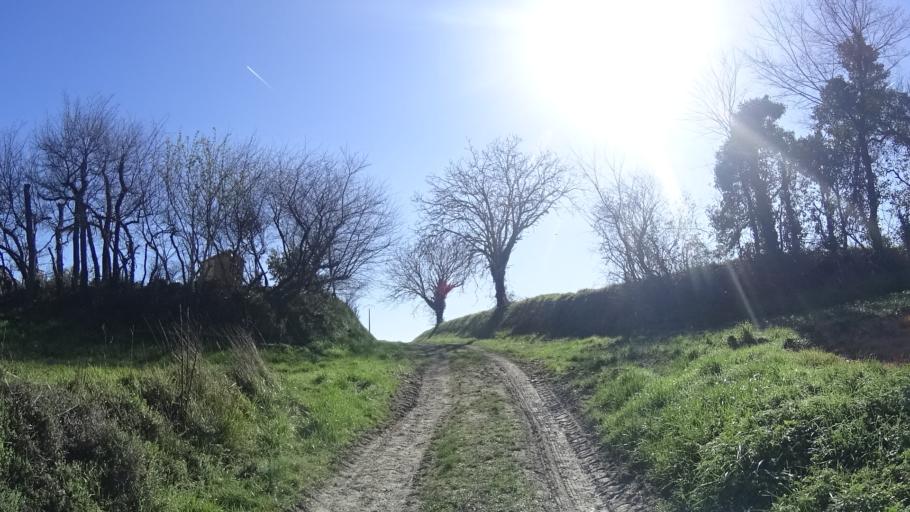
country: FR
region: Aquitaine
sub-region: Departement de la Dordogne
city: Saint-Aulaye
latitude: 45.2434
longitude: 0.1455
